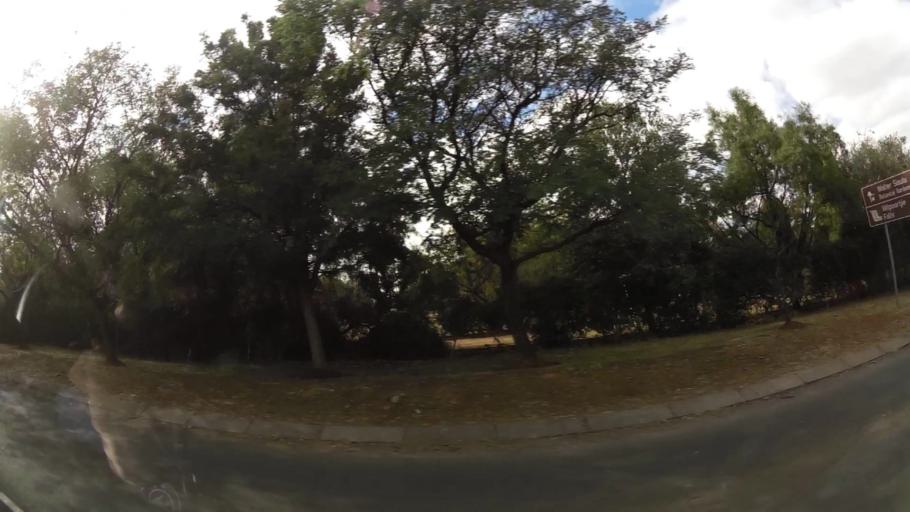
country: ZA
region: Gauteng
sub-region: West Rand District Municipality
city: Muldersdriseloop
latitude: -26.0839
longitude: 27.8546
